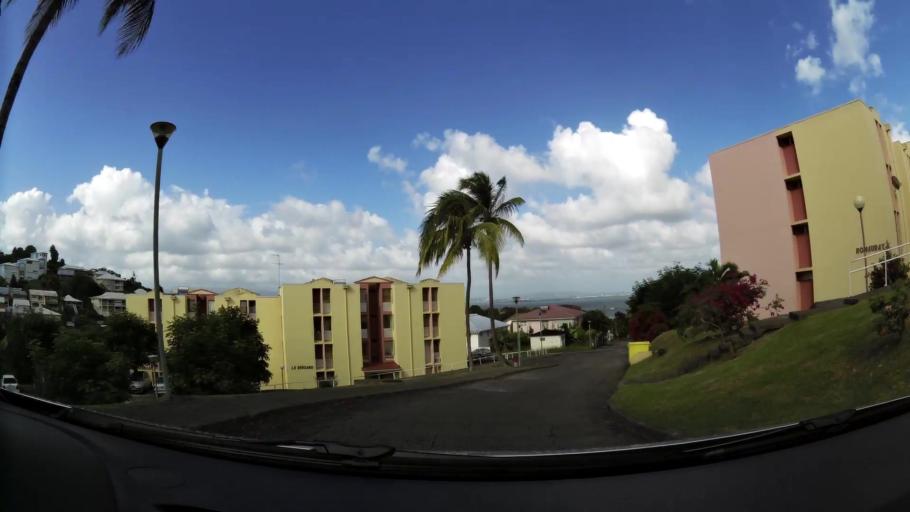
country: MQ
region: Martinique
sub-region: Martinique
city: Les Trois-Ilets
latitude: 14.5379
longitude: -61.0377
